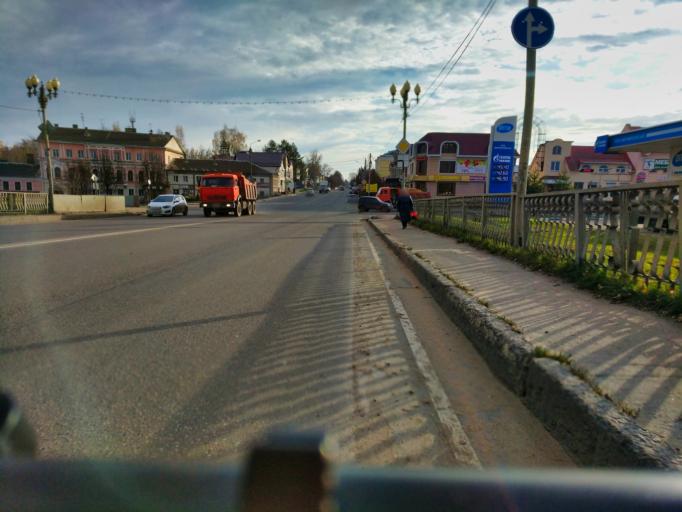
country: RU
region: Tverskaya
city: Rzhev
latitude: 56.2591
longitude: 34.3284
